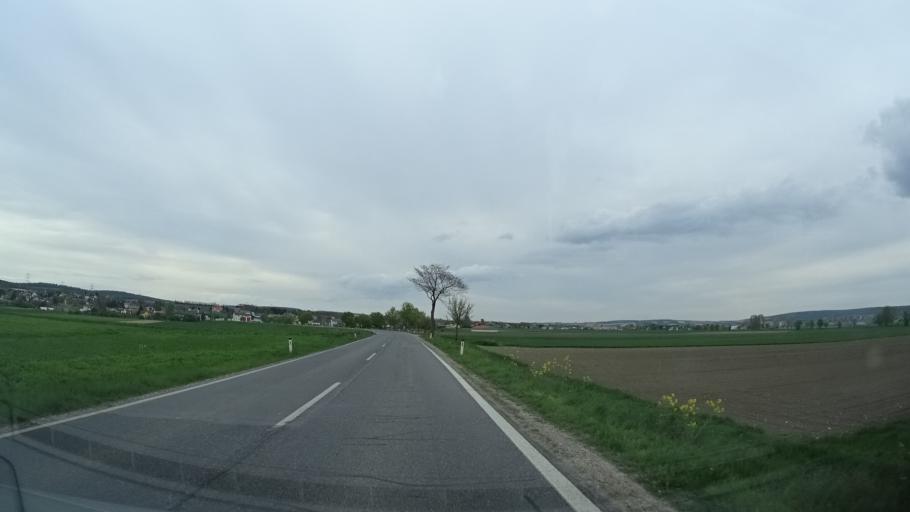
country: AT
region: Lower Austria
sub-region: Politischer Bezirk Korneuburg
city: Harmannsdorf
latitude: 48.3747
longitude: 16.3612
